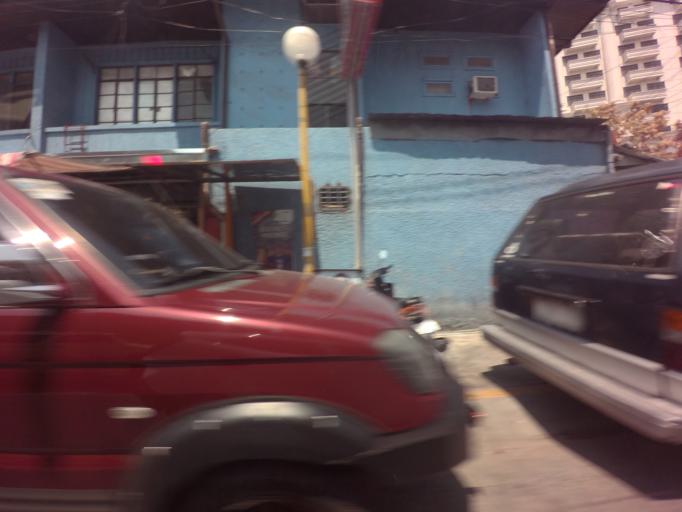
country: PH
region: Metro Manila
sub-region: City of Manila
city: Port Area
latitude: 14.5660
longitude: 120.9983
